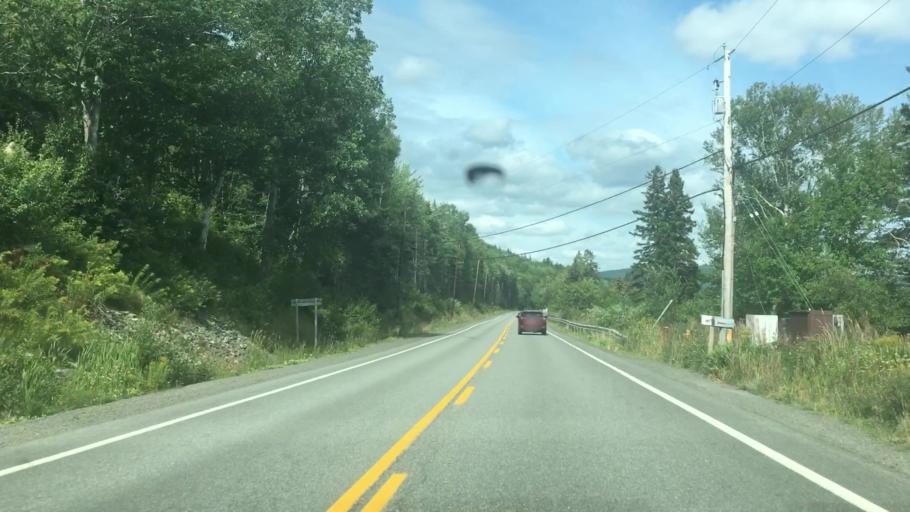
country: CA
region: Nova Scotia
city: Sydney Mines
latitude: 46.2732
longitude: -60.6100
